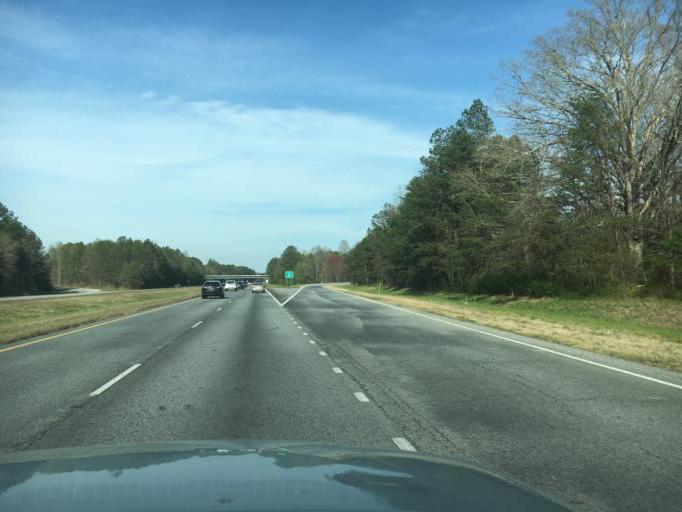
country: US
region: Georgia
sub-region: Habersham County
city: Baldwin
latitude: 34.5119
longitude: -83.5590
